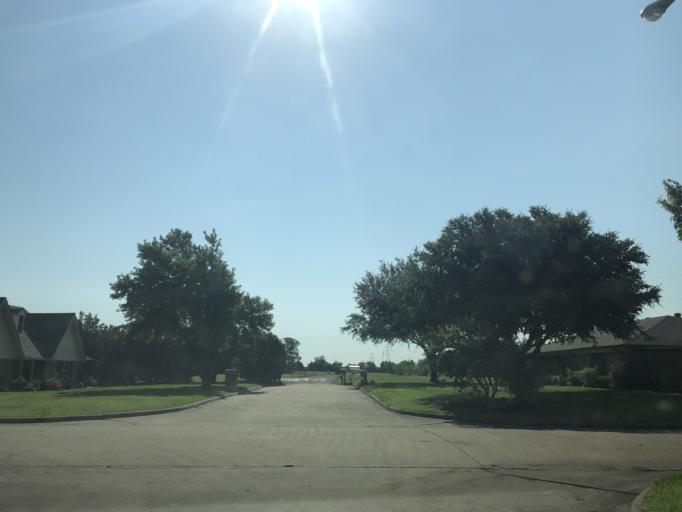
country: US
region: Texas
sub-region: Dallas County
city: Sunnyvale
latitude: 32.8210
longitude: -96.5924
